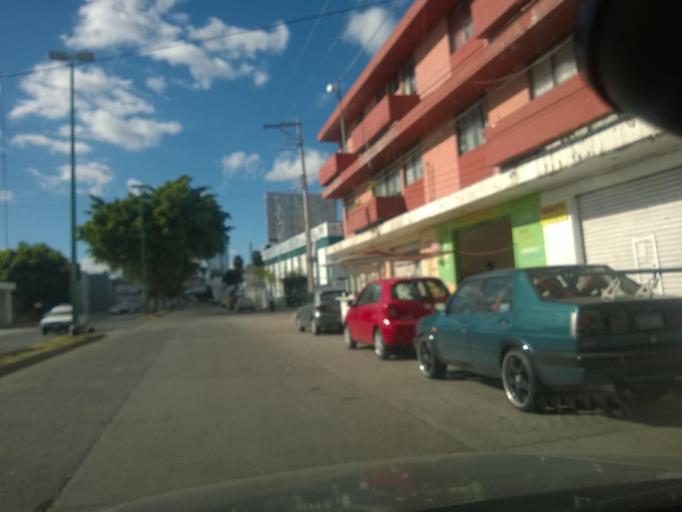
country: MX
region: Guanajuato
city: Leon
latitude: 21.1396
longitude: -101.6849
